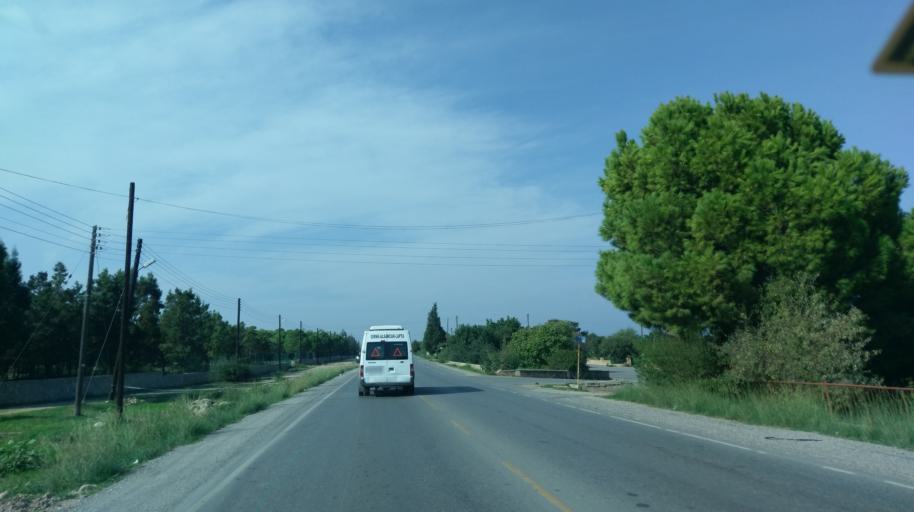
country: CY
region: Keryneia
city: Lapithos
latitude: 35.3438
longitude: 33.2405
